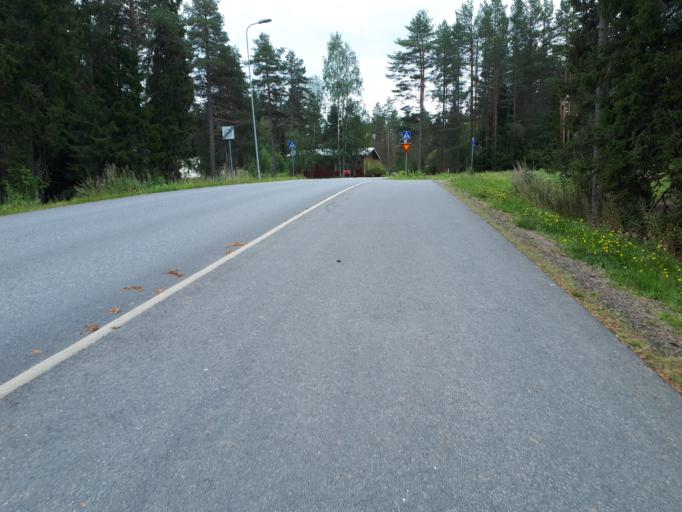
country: FI
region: Northern Ostrobothnia
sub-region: Oulunkaari
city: Ii
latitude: 65.3198
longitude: 25.4102
